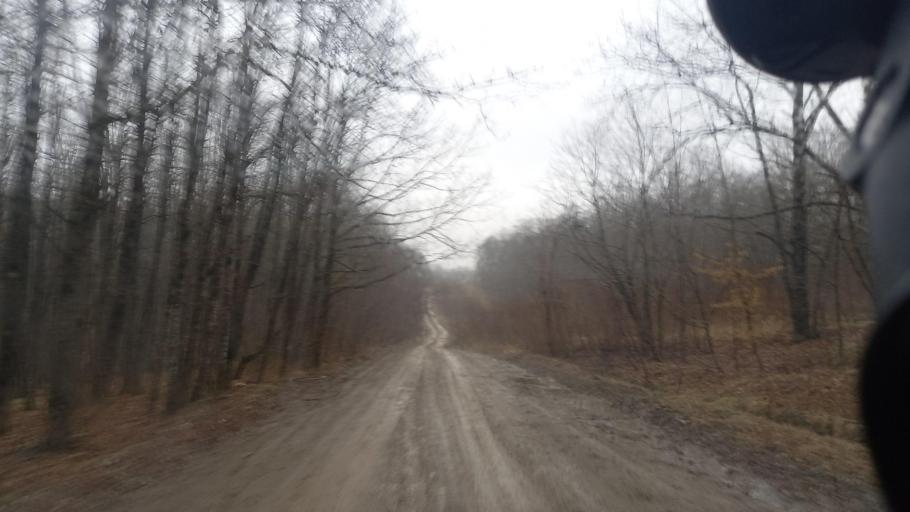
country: RU
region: Krasnodarskiy
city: Saratovskaya
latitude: 44.6453
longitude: 39.2522
